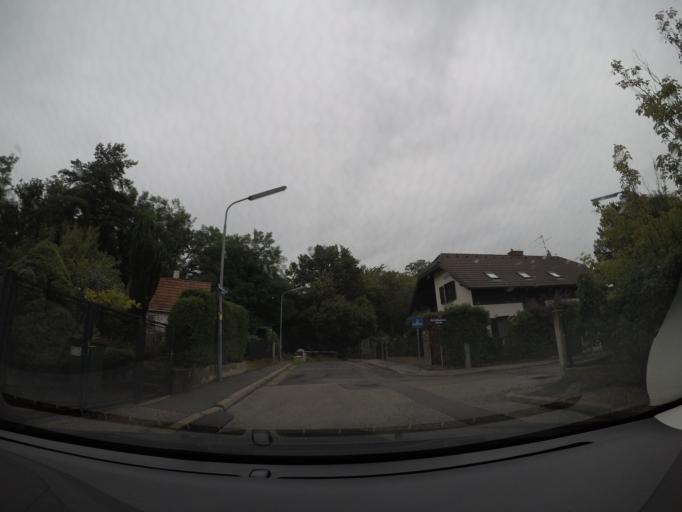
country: AT
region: Lower Austria
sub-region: Politischer Bezirk Modling
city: Perchtoldsdorf
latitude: 48.1696
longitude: 16.2612
